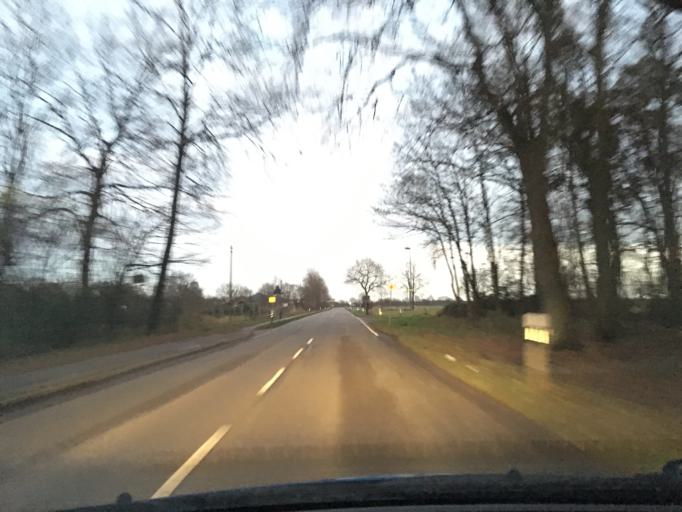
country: DE
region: Lower Saxony
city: Barum
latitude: 53.3471
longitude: 10.4177
